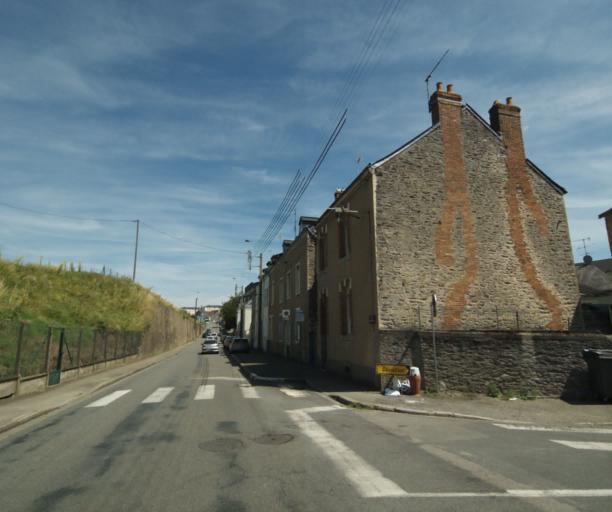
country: FR
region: Pays de la Loire
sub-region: Departement de la Mayenne
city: Laval
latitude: 48.0756
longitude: -0.7577
